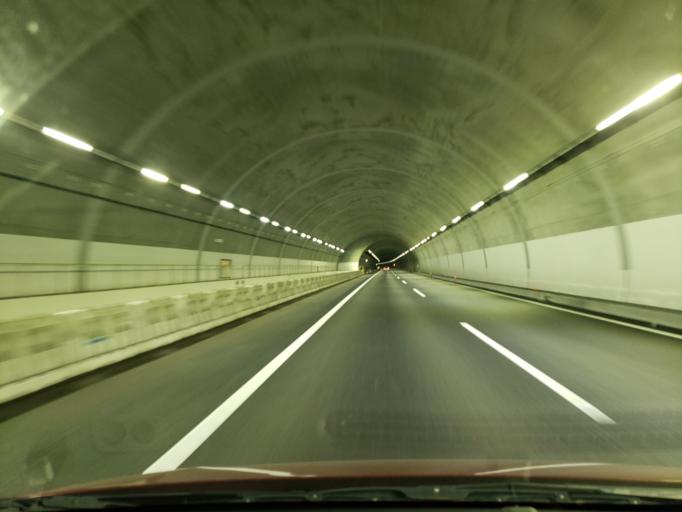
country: JP
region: Osaka
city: Ikeda
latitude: 34.8809
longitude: 135.4097
